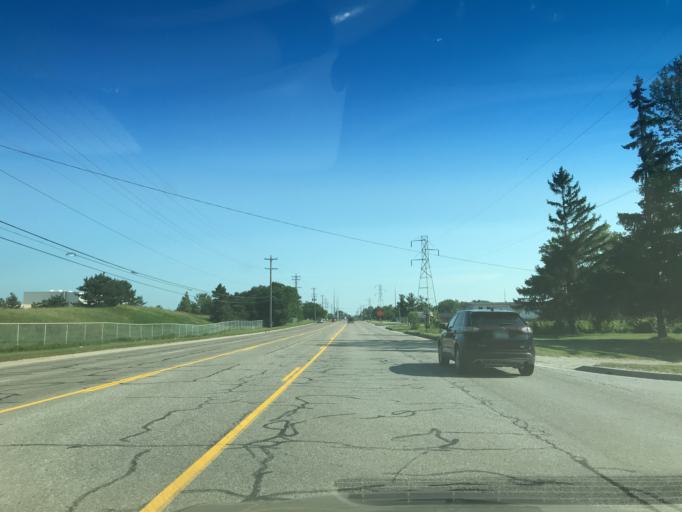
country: US
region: Michigan
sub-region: Eaton County
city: Waverly
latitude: 42.7038
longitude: -84.6424
